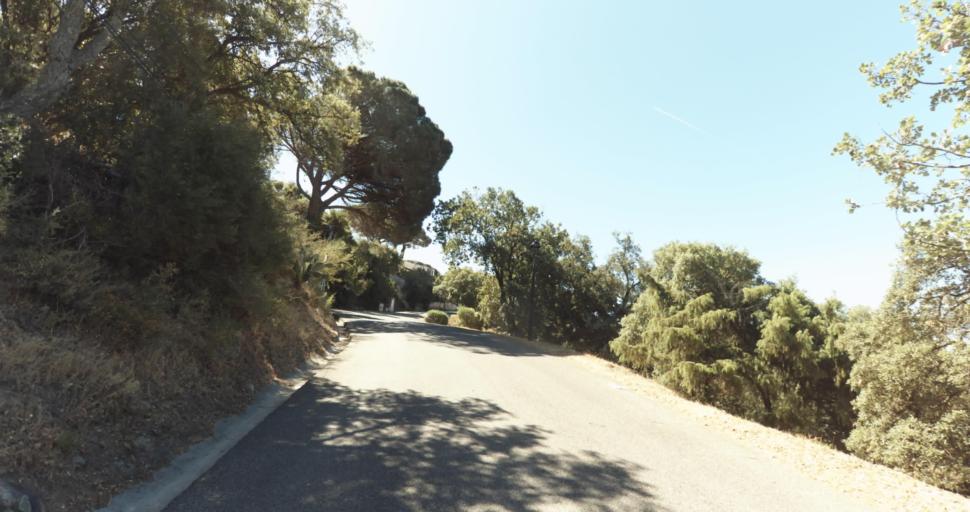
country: FR
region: Provence-Alpes-Cote d'Azur
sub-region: Departement du Var
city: Gassin
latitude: 43.2584
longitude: 6.6027
